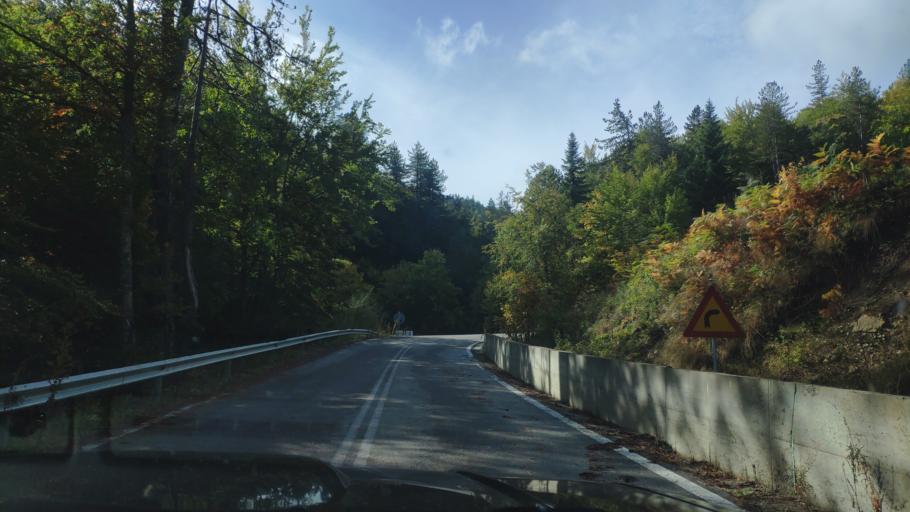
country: AL
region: Korce
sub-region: Rrethi i Devollit
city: Miras
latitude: 40.3667
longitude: 20.9263
